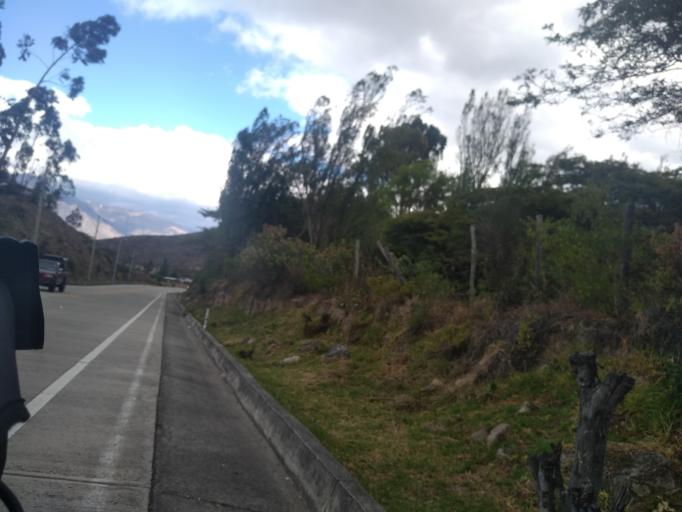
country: EC
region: El Oro
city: Zaruma
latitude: -3.4096
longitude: -79.1790
